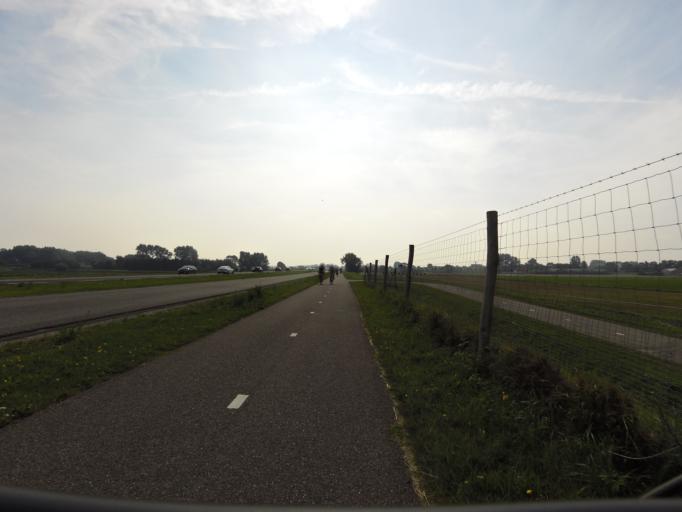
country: NL
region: Zeeland
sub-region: Gemeente Veere
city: Veere
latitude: 51.5817
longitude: 3.6236
